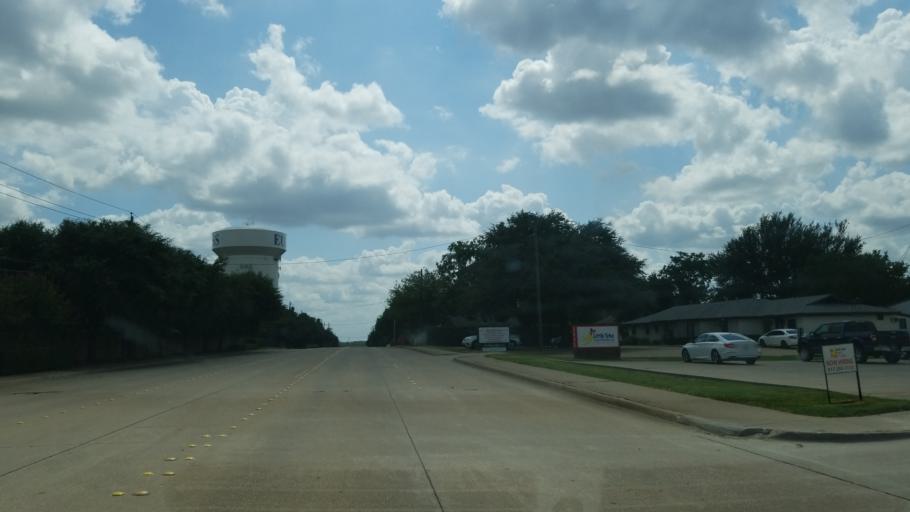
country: US
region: Texas
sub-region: Tarrant County
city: Euless
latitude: 32.8804
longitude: -97.0824
